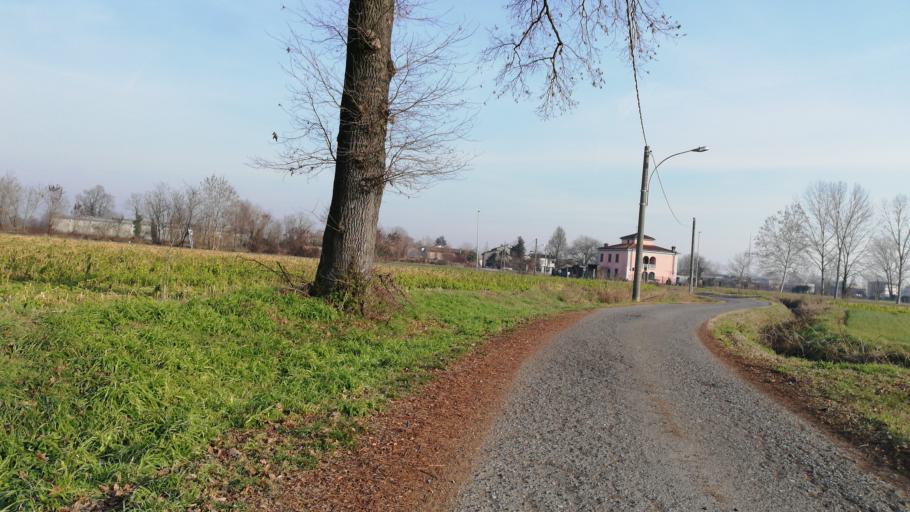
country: IT
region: Lombardy
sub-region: Provincia di Cremona
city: Crema
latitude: 45.3806
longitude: 9.6771
